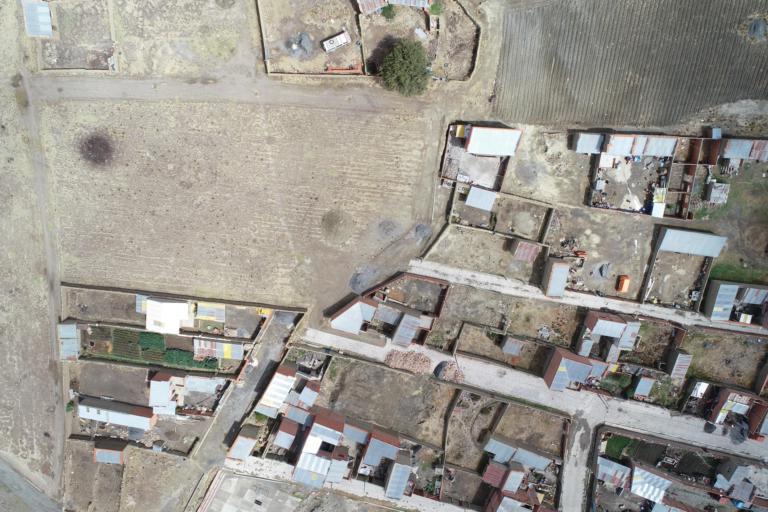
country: BO
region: La Paz
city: Achacachi
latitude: -16.0339
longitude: -68.6894
